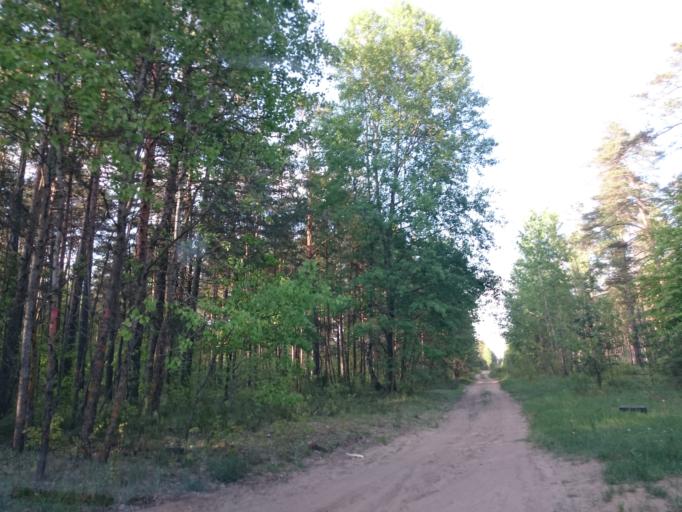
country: LV
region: Stopini
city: Ulbroka
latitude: 56.9506
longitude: 24.2883
